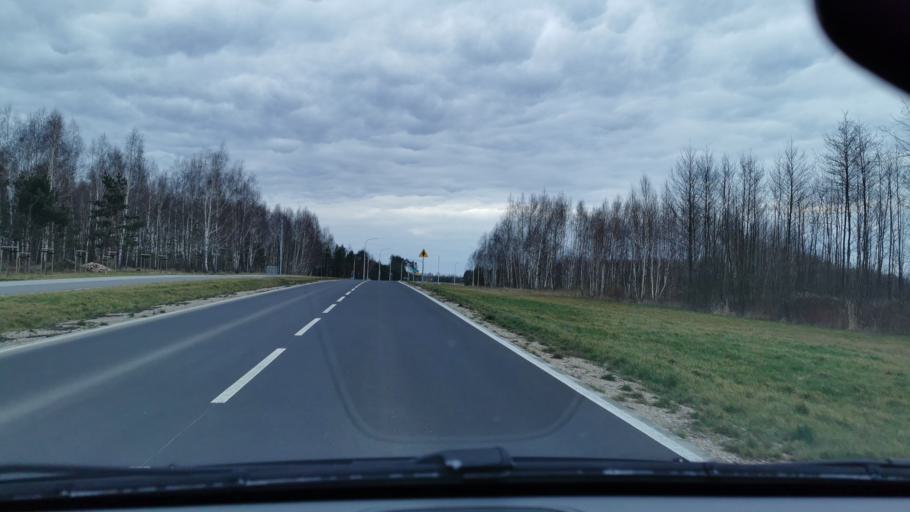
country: PL
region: Masovian Voivodeship
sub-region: Powiat zyrardowski
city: Zyrardow
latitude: 52.0046
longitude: 20.4645
